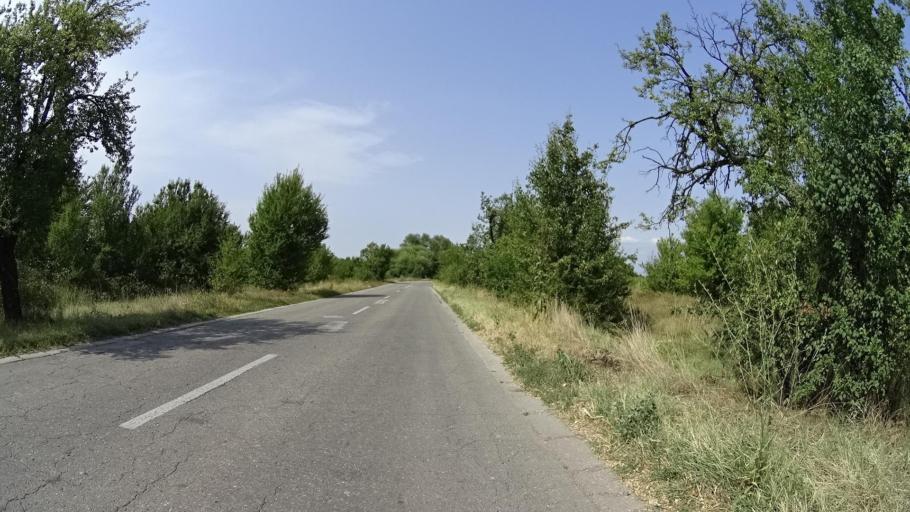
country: BG
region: Plovdiv
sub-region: Obshtina Plovdiv
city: Plovdiv
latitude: 42.2313
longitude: 24.7859
